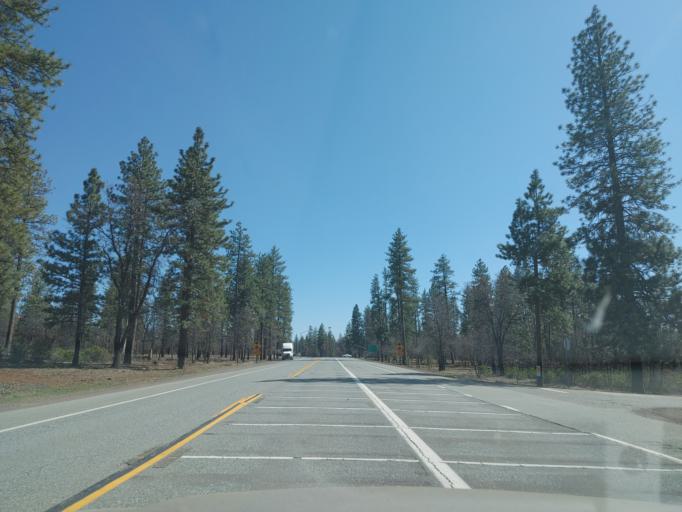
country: US
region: California
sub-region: Shasta County
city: Burney
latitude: 40.9405
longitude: -121.6076
